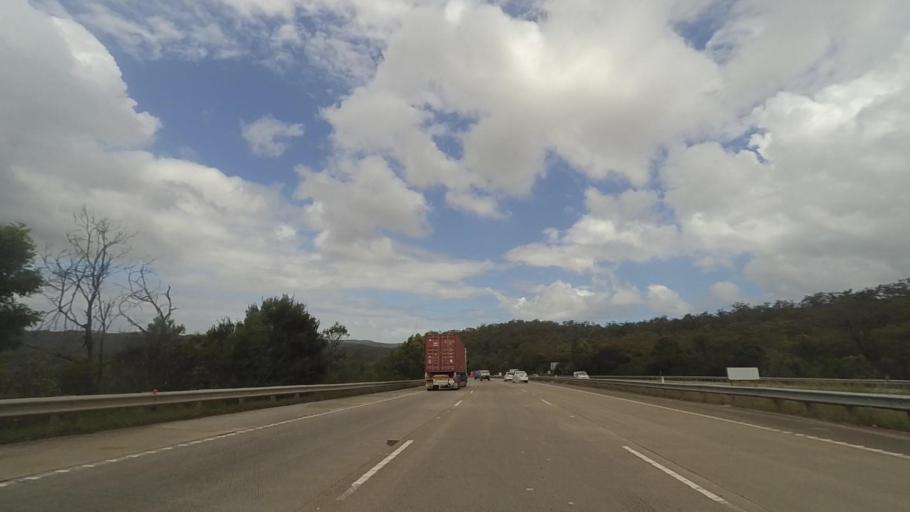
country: AU
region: New South Wales
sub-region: Gosford Shire
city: Point Clare
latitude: -33.4280
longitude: 151.2396
